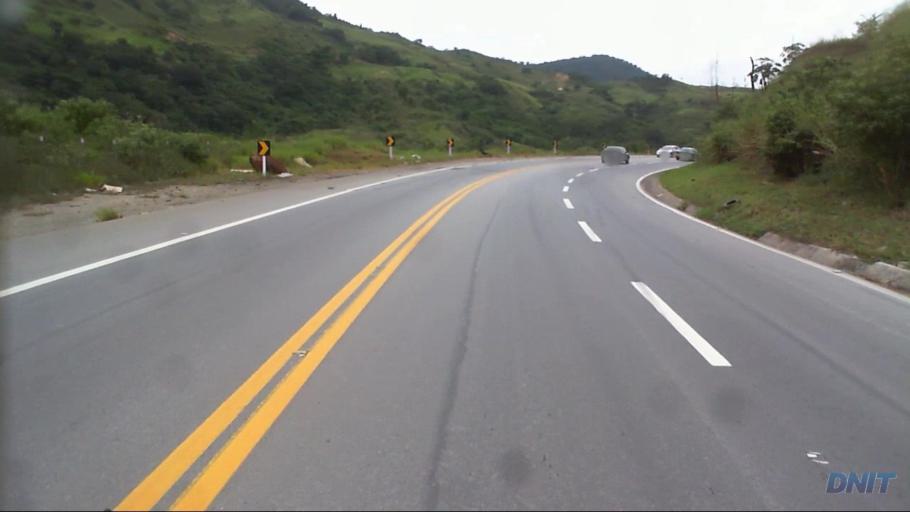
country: BR
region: Minas Gerais
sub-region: Timoteo
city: Timoteo
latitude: -19.6370
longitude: -42.8074
